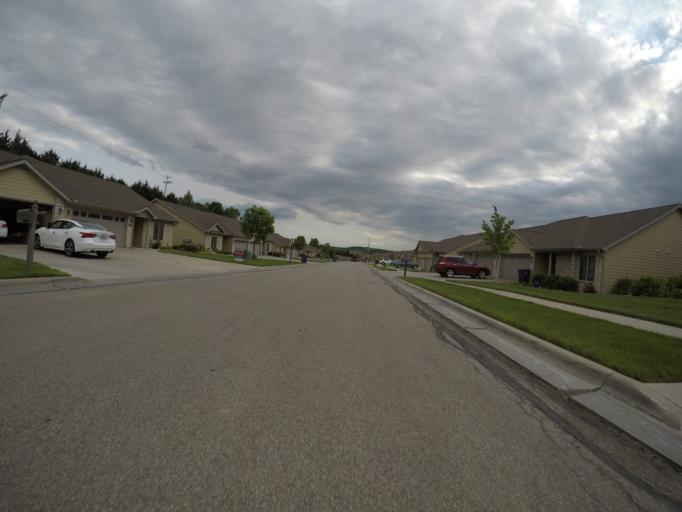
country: US
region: Kansas
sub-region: Riley County
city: Manhattan
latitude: 39.1952
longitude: -96.6403
